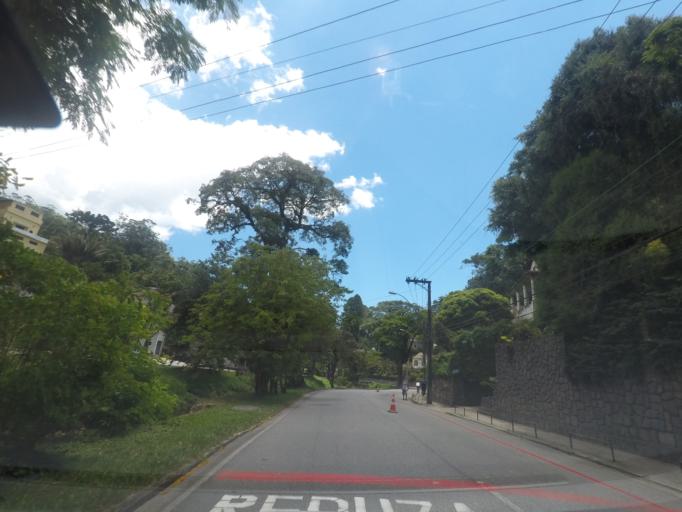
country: BR
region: Rio de Janeiro
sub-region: Petropolis
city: Petropolis
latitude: -22.4995
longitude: -43.1805
